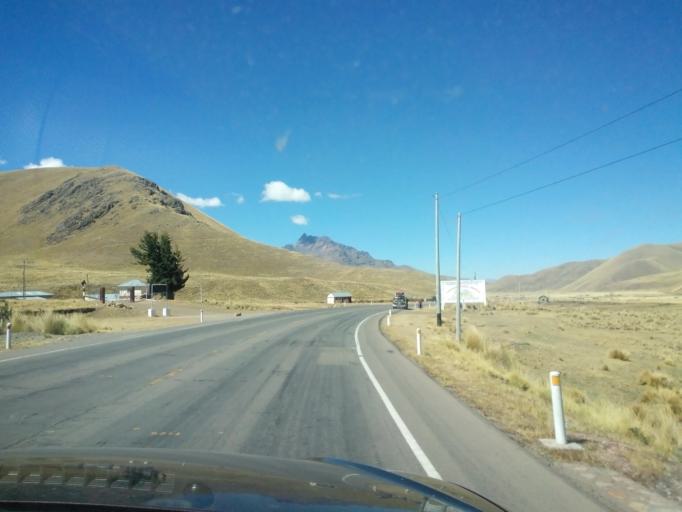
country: PE
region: Puno
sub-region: Provincia de Melgar
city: Santa Rosa
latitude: -14.4965
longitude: -70.9412
